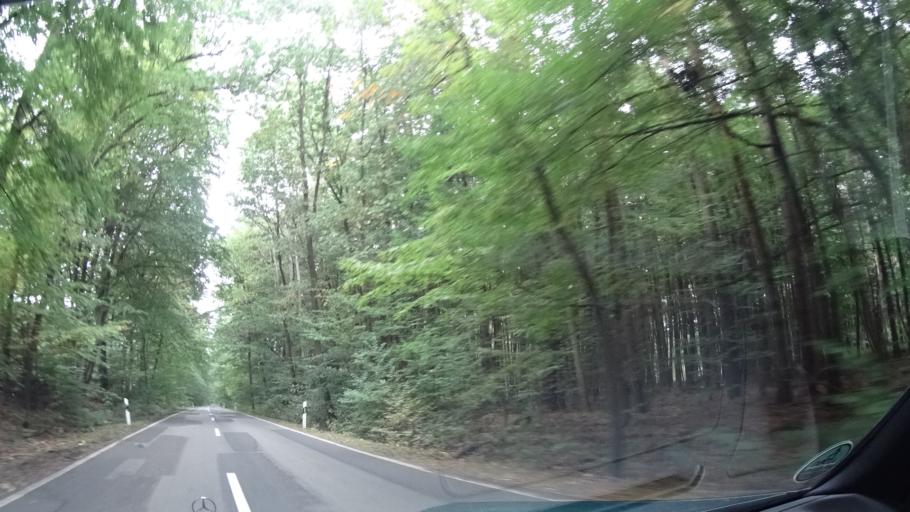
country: DE
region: Brandenburg
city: Walsleben
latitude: 52.9701
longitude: 12.7165
